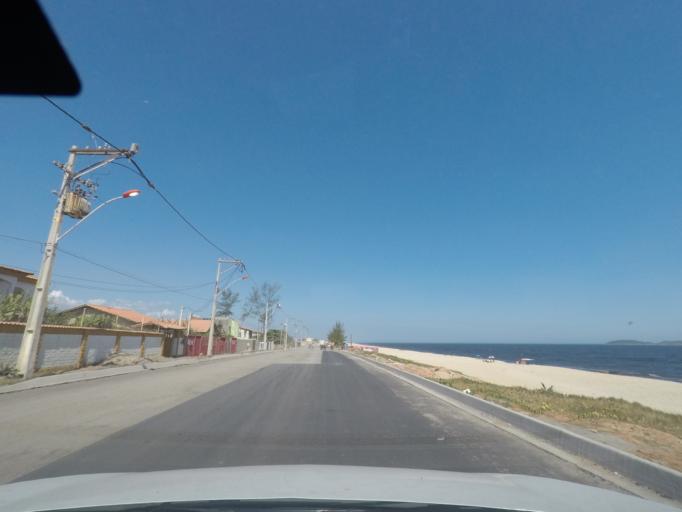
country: BR
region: Rio de Janeiro
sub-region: Marica
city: Marica
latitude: -22.9705
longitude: -42.9544
